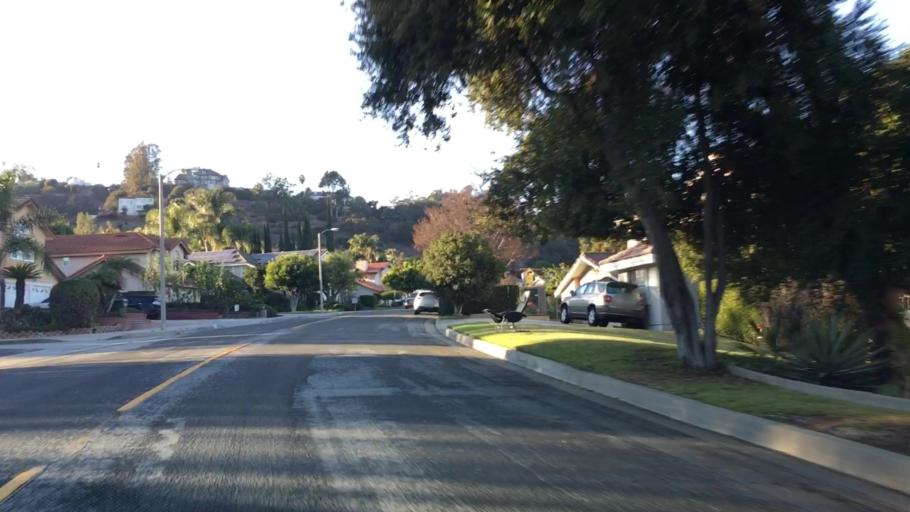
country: US
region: California
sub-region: Los Angeles County
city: Hacienda Heights
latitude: 33.9912
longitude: -117.9869
